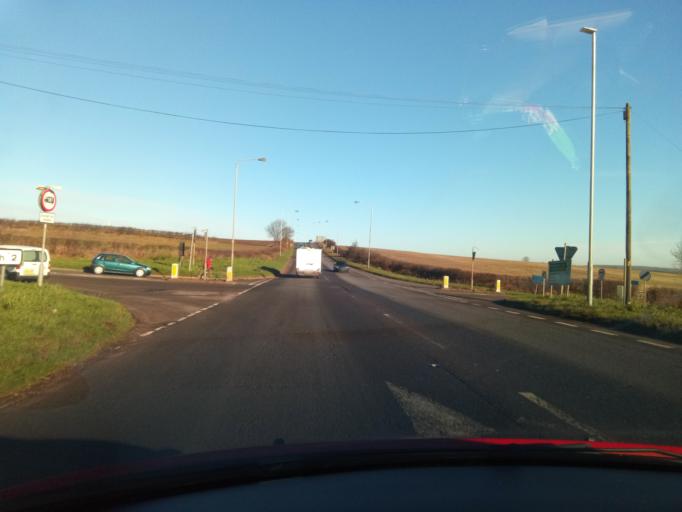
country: GB
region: England
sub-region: Nottinghamshire
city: Farnsfield
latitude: 53.0944
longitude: -1.0683
